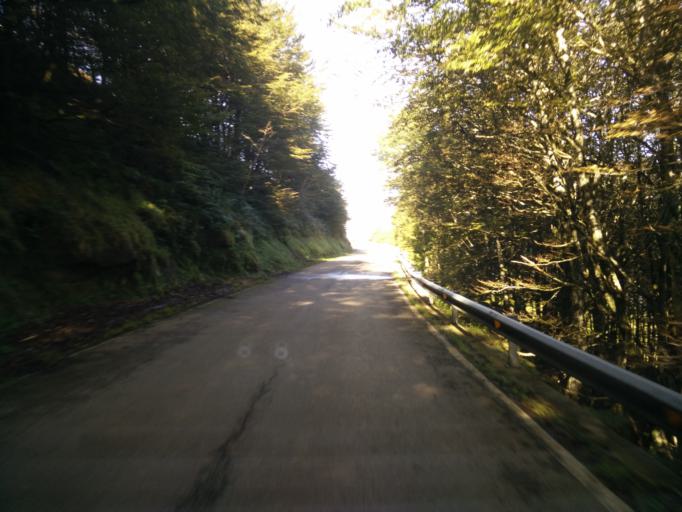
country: ES
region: Cantabria
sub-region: Provincia de Cantabria
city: San Pedro del Romeral
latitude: 43.0520
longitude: -3.8462
